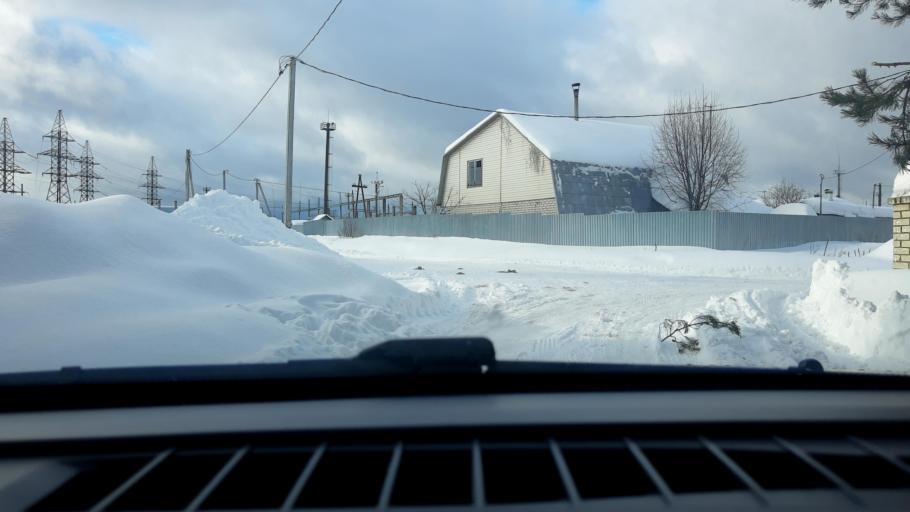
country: RU
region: Nizjnij Novgorod
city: Lukino
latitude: 56.3955
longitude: 43.7084
